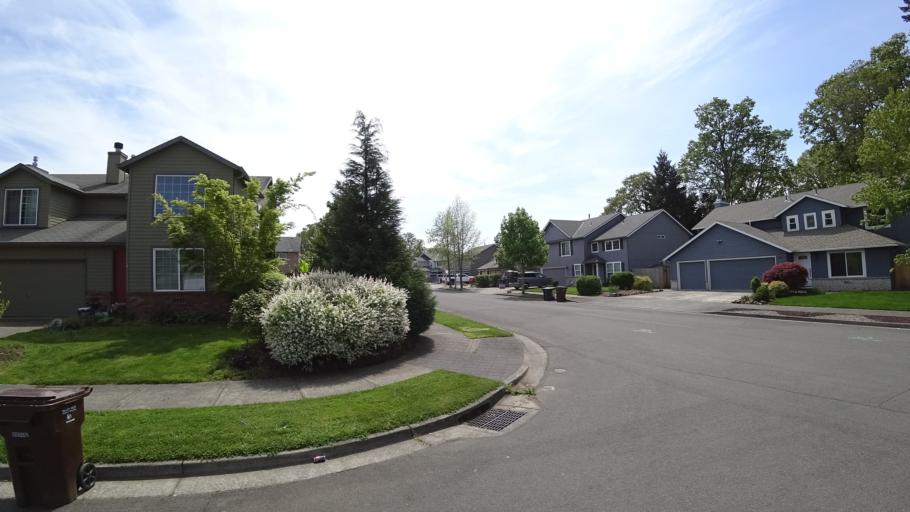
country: US
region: Oregon
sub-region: Washington County
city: Rockcreek
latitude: 45.5138
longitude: -122.9192
